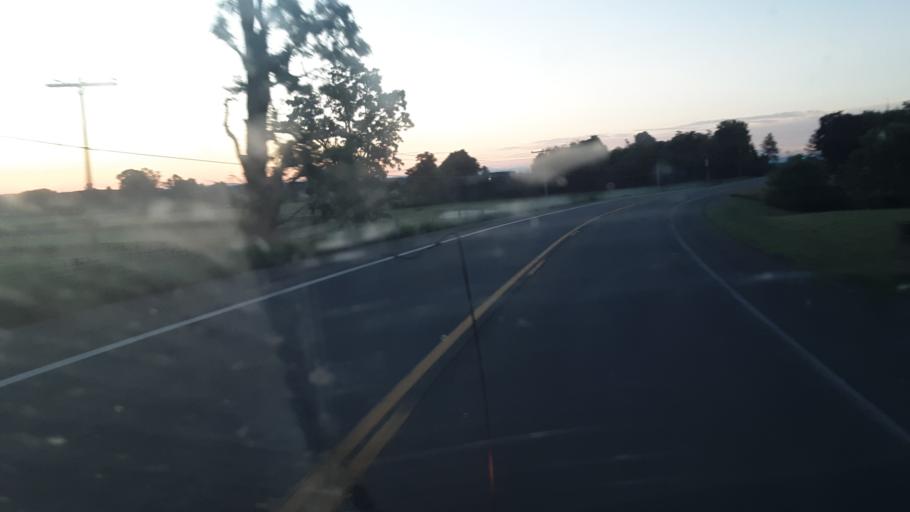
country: US
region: New York
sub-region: Montgomery County
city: Hagaman
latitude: 42.9744
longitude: -74.0351
